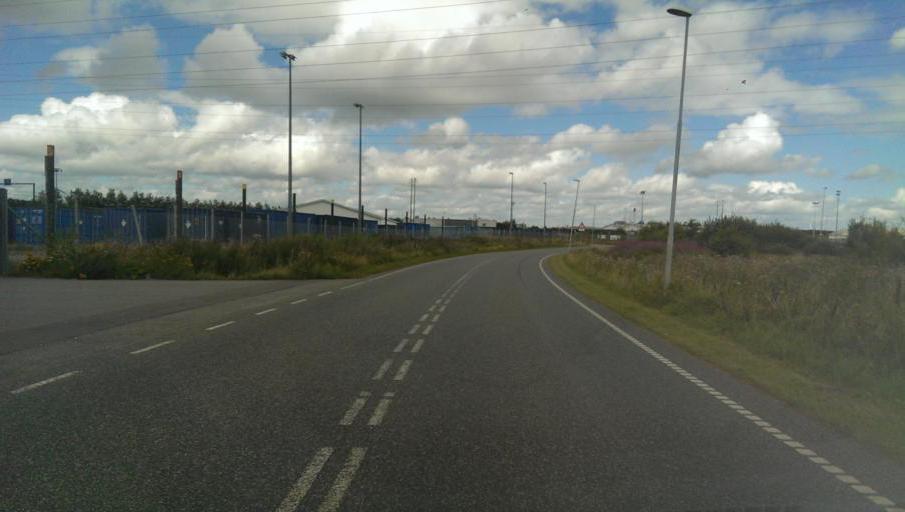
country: DK
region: South Denmark
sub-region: Esbjerg Kommune
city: Esbjerg
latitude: 55.4631
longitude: 8.5073
